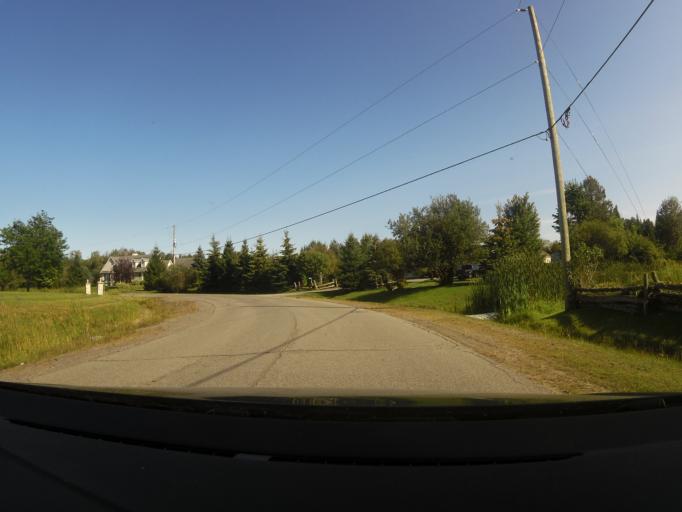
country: CA
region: Ontario
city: Carleton Place
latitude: 45.2907
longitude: -76.0708
